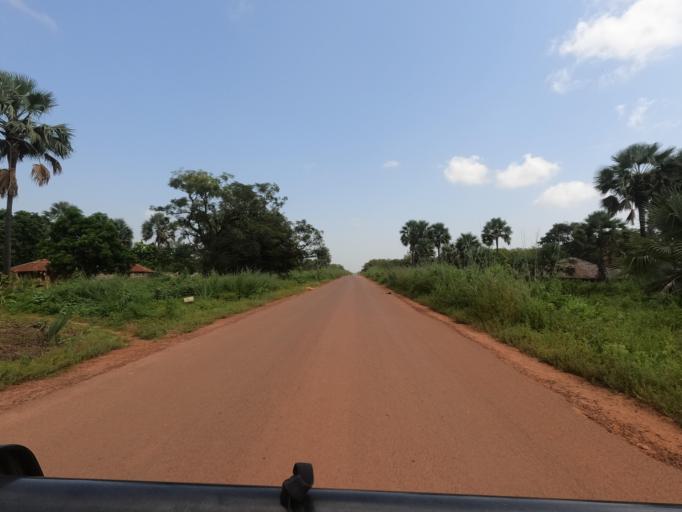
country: GW
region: Oio
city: Bissora
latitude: 12.2953
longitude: -15.7682
